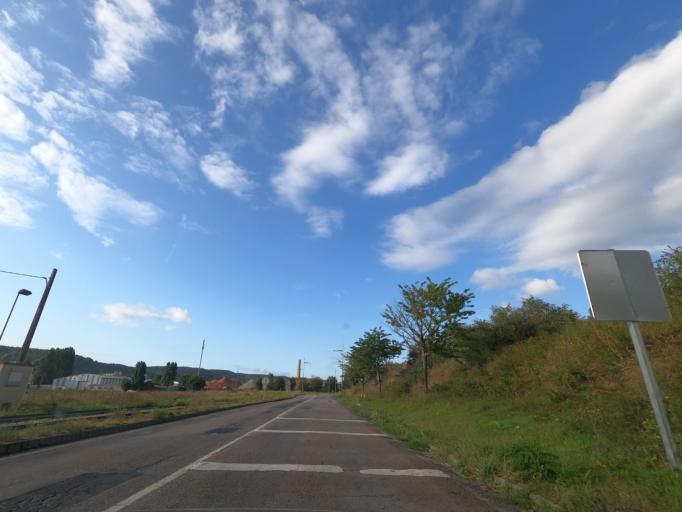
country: FR
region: Haute-Normandie
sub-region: Departement de la Seine-Maritime
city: Petit-Couronne
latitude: 49.3990
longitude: 1.0193
